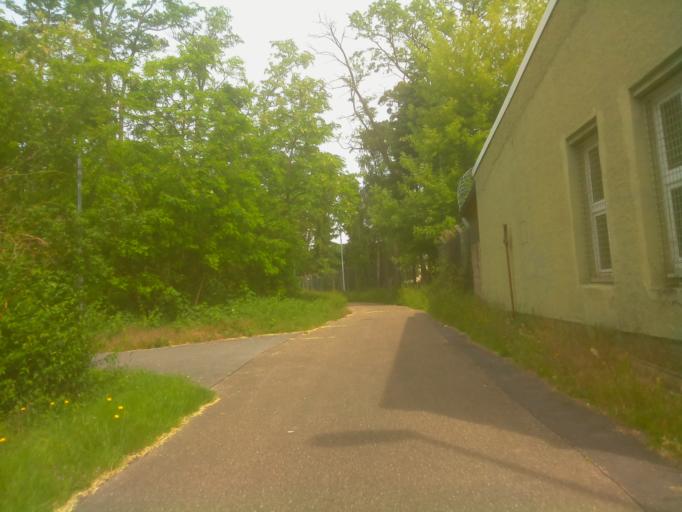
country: DE
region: Hesse
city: Viernheim
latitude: 49.5166
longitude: 8.5485
